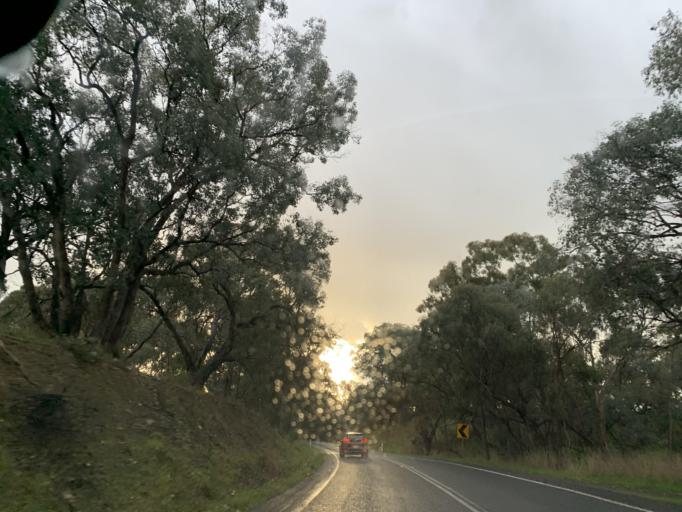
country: AU
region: Victoria
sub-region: Murrindindi
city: Kinglake West
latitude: -37.2178
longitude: 145.1100
